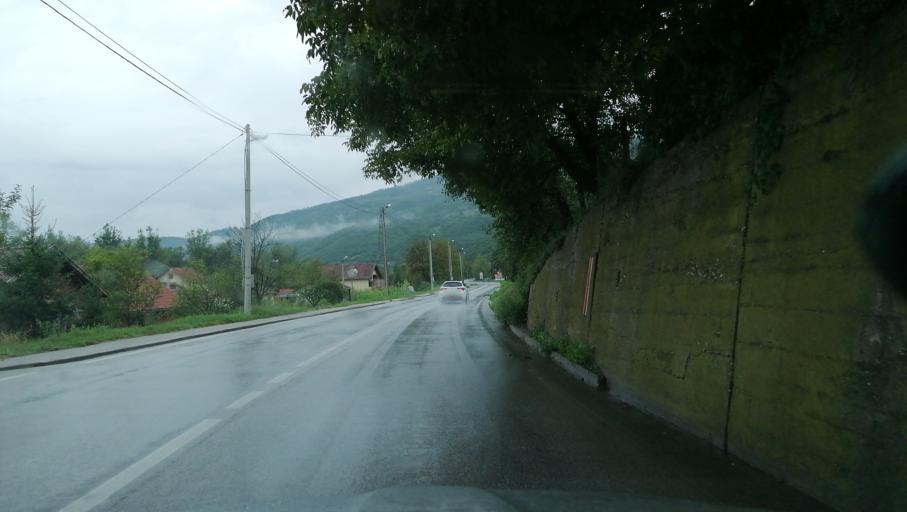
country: BA
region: Federation of Bosnia and Herzegovina
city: Gorazde
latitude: 43.6813
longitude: 19.0108
